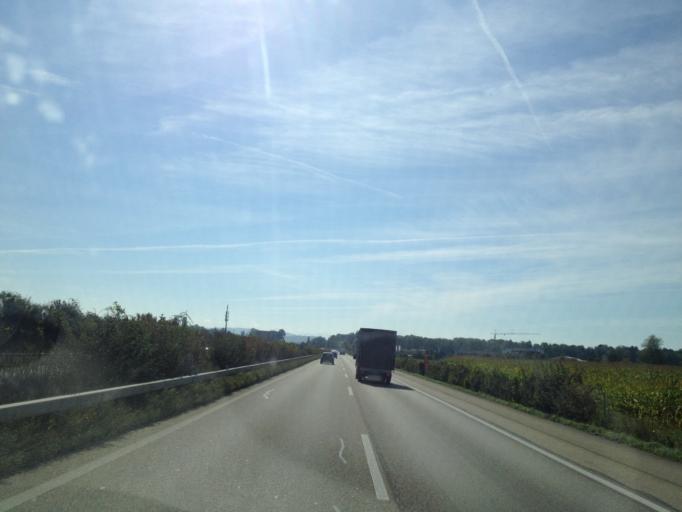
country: CH
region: Bern
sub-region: Emmental District
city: Kirchberg
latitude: 47.0998
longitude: 7.5747
